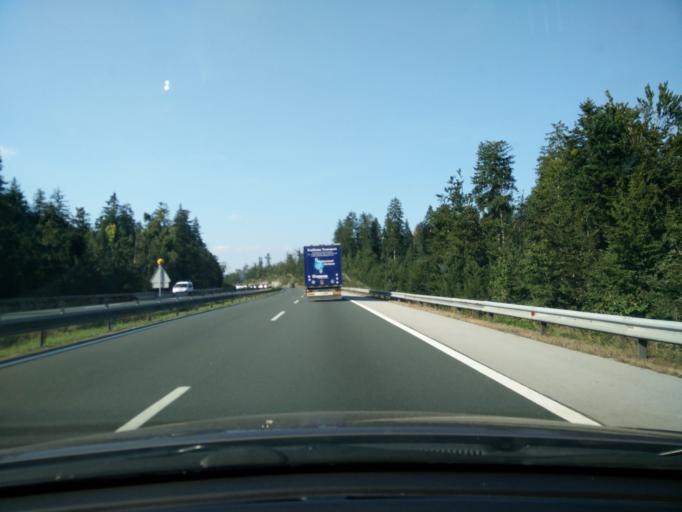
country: SI
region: Logatec
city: Logatec
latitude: 45.8796
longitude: 14.2629
